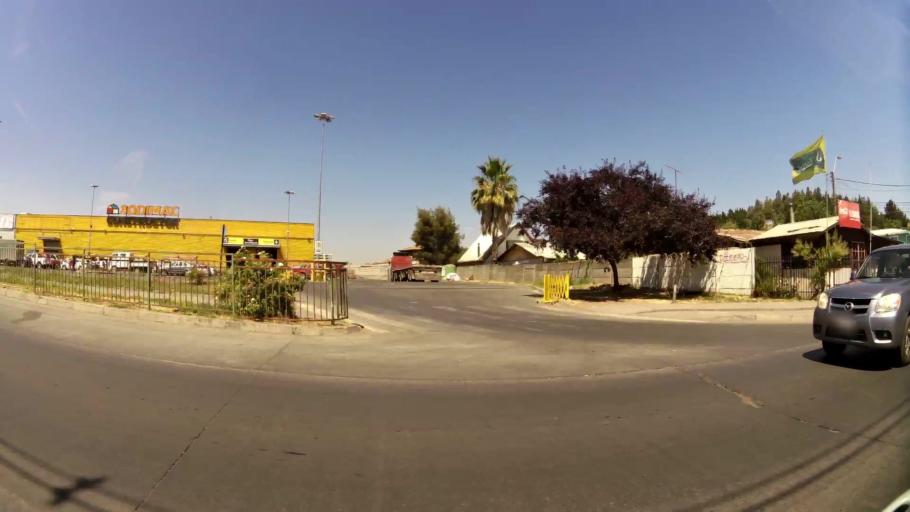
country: CL
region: Maule
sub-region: Provincia de Curico
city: Curico
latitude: -34.9763
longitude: -71.2218
